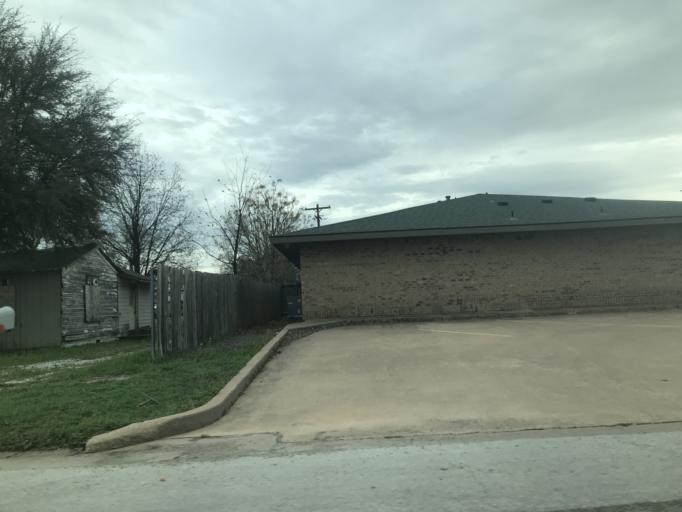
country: US
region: Texas
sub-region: Taylor County
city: Abilene
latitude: 32.4673
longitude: -99.7342
